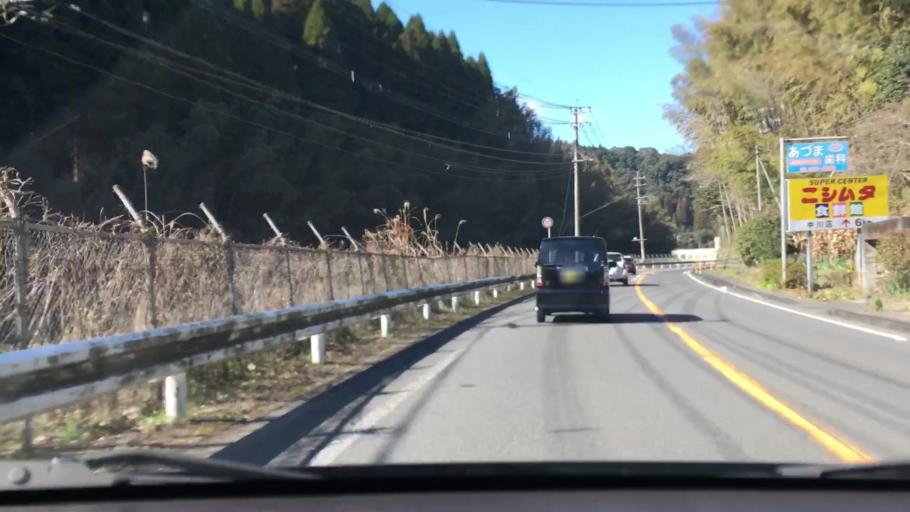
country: JP
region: Kagoshima
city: Ijuin
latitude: 31.6523
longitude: 130.4999
